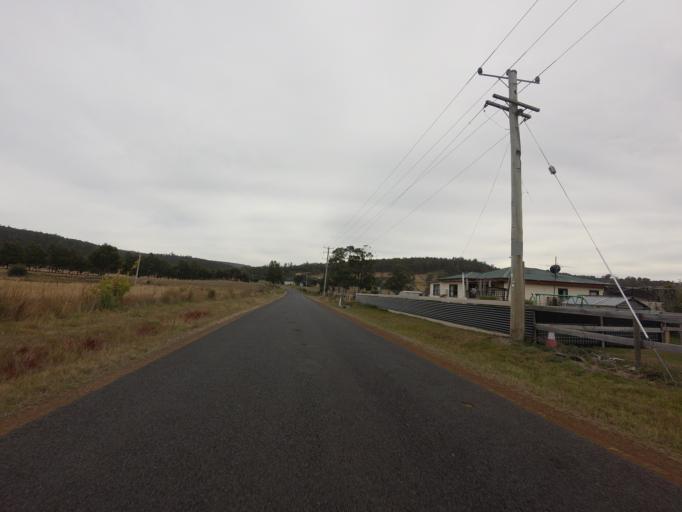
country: AU
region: Tasmania
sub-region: Sorell
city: Sorell
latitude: -42.5646
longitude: 147.5719
